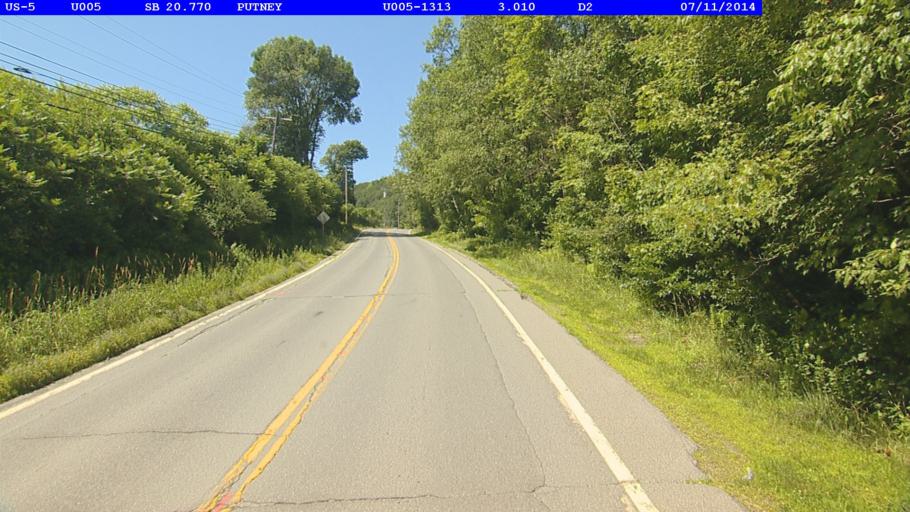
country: US
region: New Hampshire
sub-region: Cheshire County
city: Westmoreland
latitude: 42.9993
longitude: -72.4917
